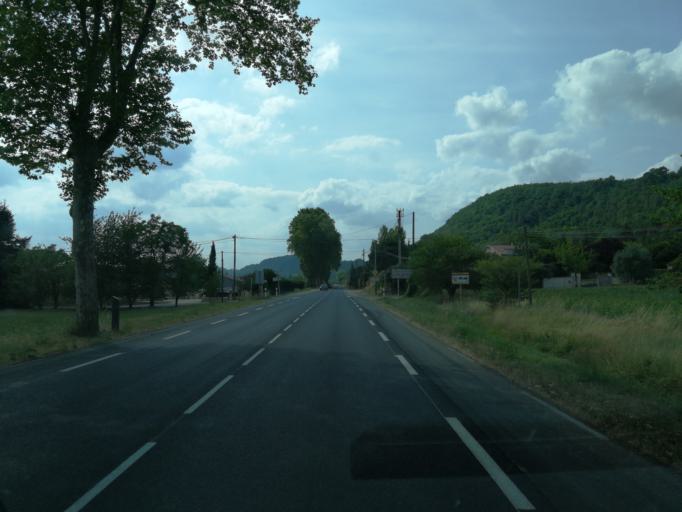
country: FR
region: Aquitaine
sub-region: Departement du Lot-et-Garonne
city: Montayral
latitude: 44.4920
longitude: 1.0035
